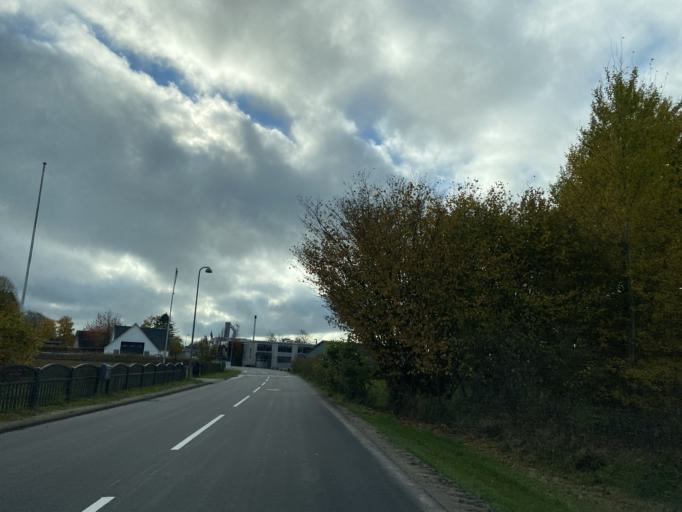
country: DK
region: Central Jutland
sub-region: Favrskov Kommune
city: Hammel
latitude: 56.2441
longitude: 9.8153
